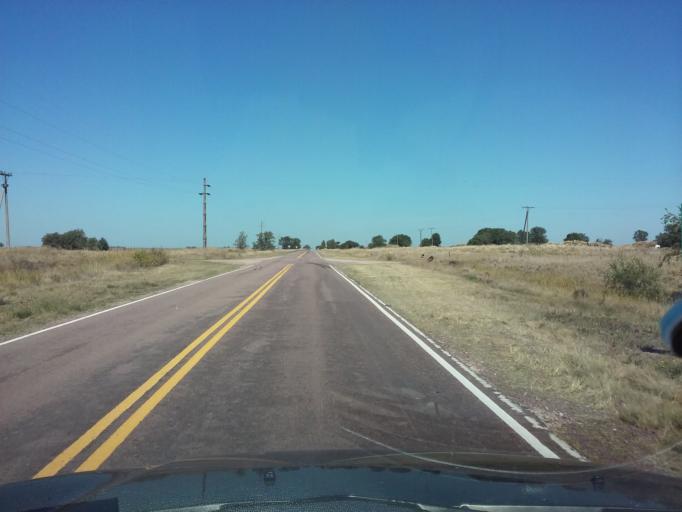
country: AR
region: La Pampa
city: Uriburu
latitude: -36.4145
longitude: -63.9431
